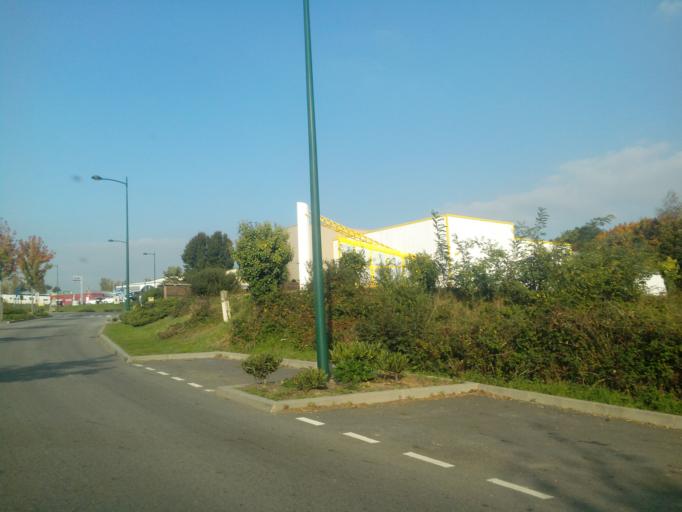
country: FR
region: Brittany
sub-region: Departement du Morbihan
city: Ploermel
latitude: 47.9290
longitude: -2.3808
